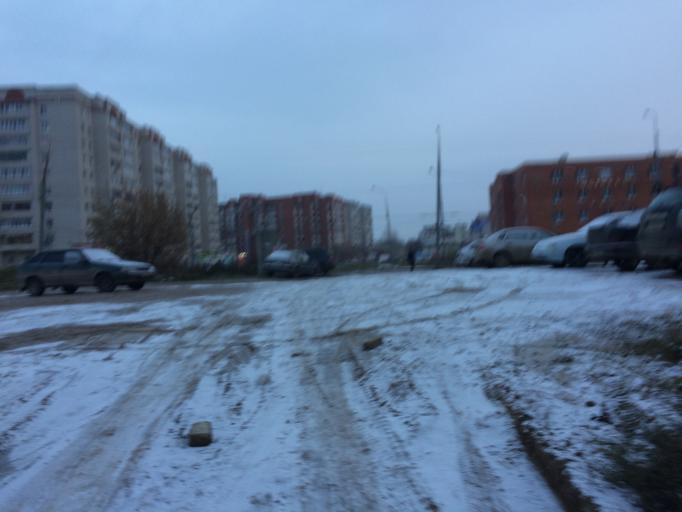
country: RU
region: Mariy-El
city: Yoshkar-Ola
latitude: 56.6378
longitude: 47.9327
